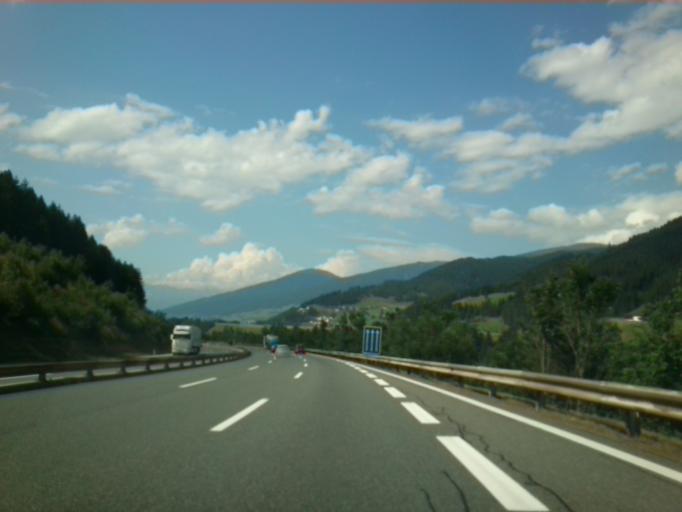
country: AT
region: Tyrol
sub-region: Politischer Bezirk Innsbruck Land
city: Steinach am Brenner
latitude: 47.0959
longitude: 11.4627
